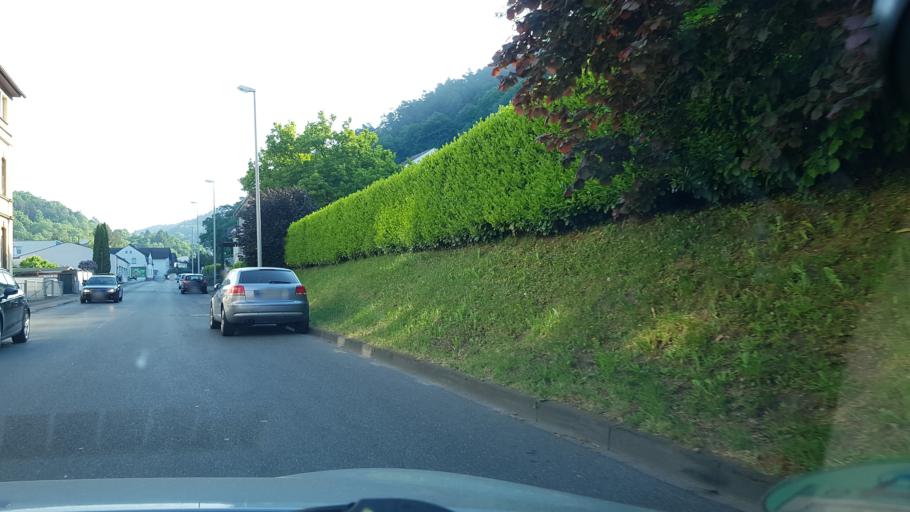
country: DE
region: Rheinland-Pfalz
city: Bad Ems
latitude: 50.3399
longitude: 7.7153
